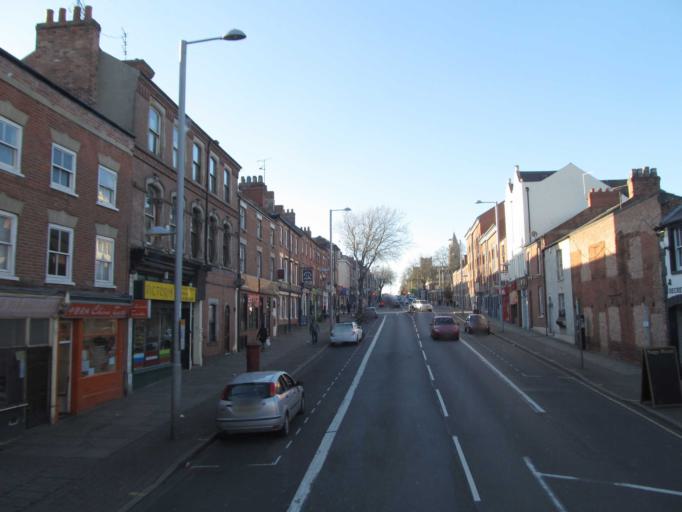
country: GB
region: England
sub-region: Nottingham
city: Nottingham
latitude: 52.9618
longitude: -1.1509
